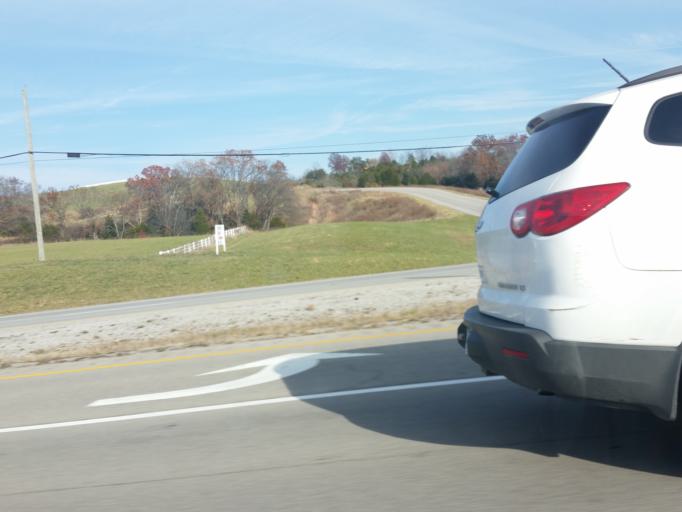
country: US
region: Kentucky
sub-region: Campbell County
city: Claryville
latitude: 38.8604
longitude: -84.3898
